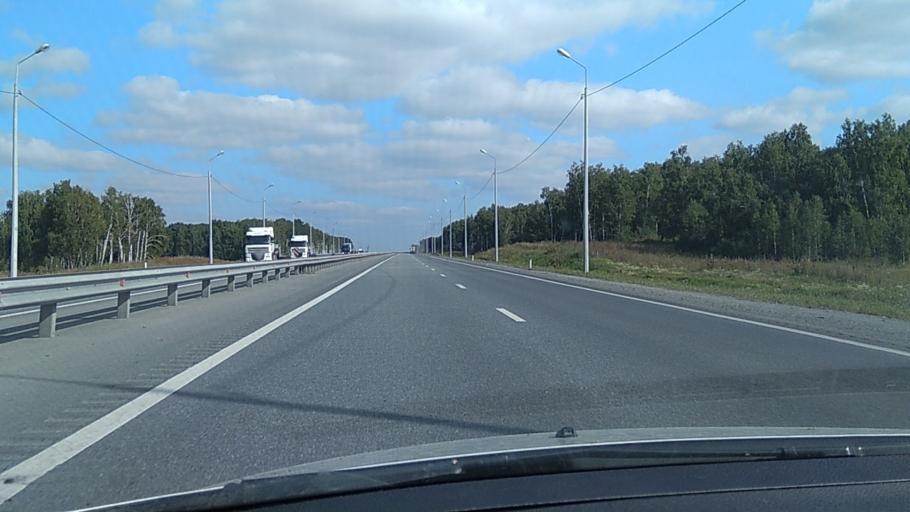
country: RU
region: Chelyabinsk
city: Chebarkul'
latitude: 54.9126
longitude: 60.3911
